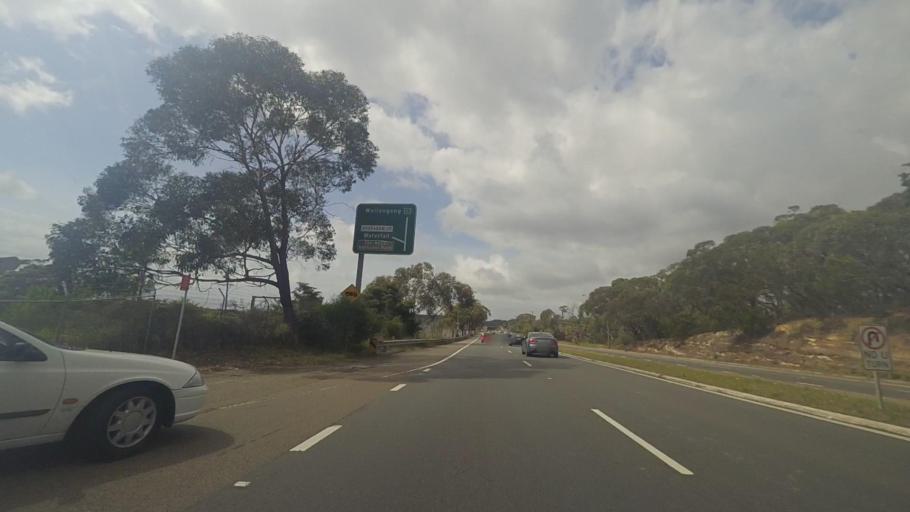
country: AU
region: New South Wales
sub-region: Wollongong
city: Helensburgh
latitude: -34.1298
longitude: 150.9935
